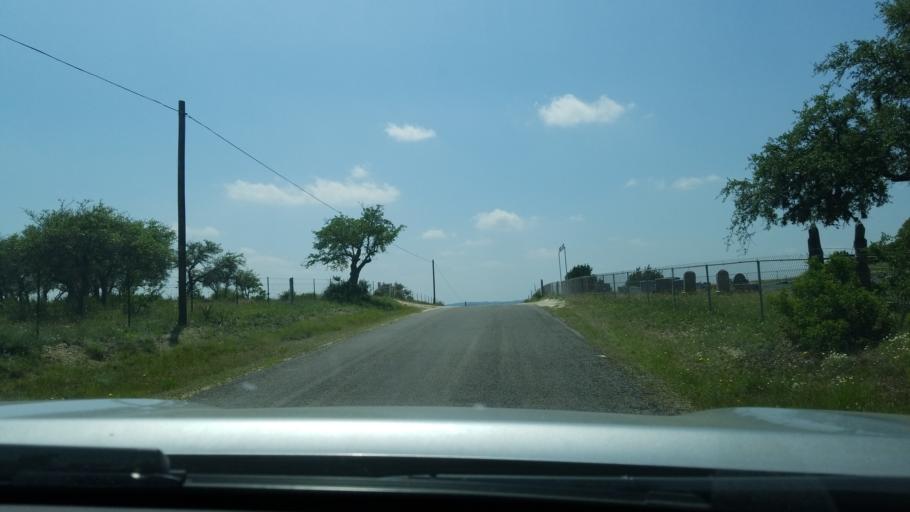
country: US
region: Texas
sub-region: Blanco County
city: Blanco
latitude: 29.9921
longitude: -98.5229
